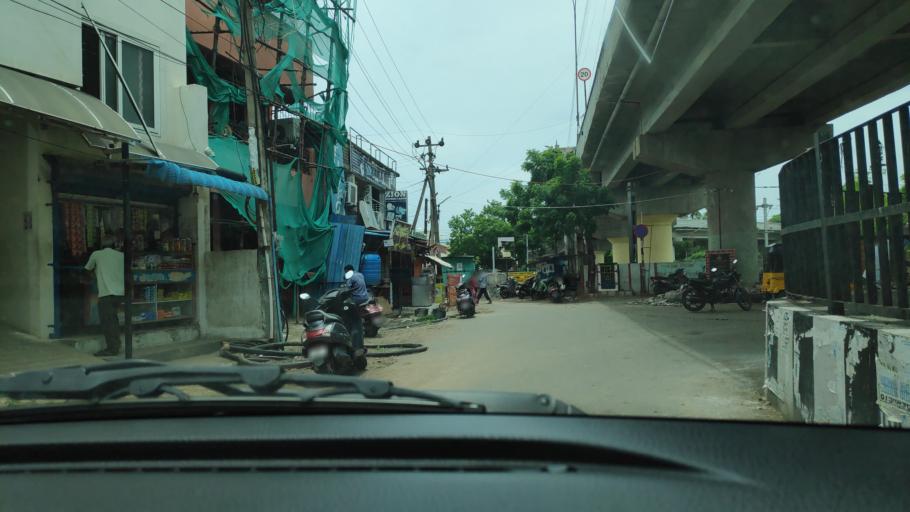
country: IN
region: Tamil Nadu
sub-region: Kancheepuram
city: Pallavaram
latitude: 12.9367
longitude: 80.1301
